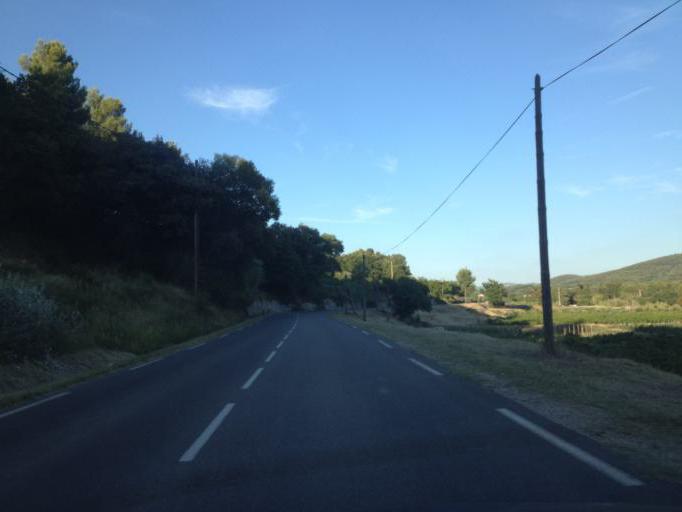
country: FR
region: Provence-Alpes-Cote d'Azur
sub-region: Departement du Vaucluse
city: Sablet
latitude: 44.2367
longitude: 5.0026
